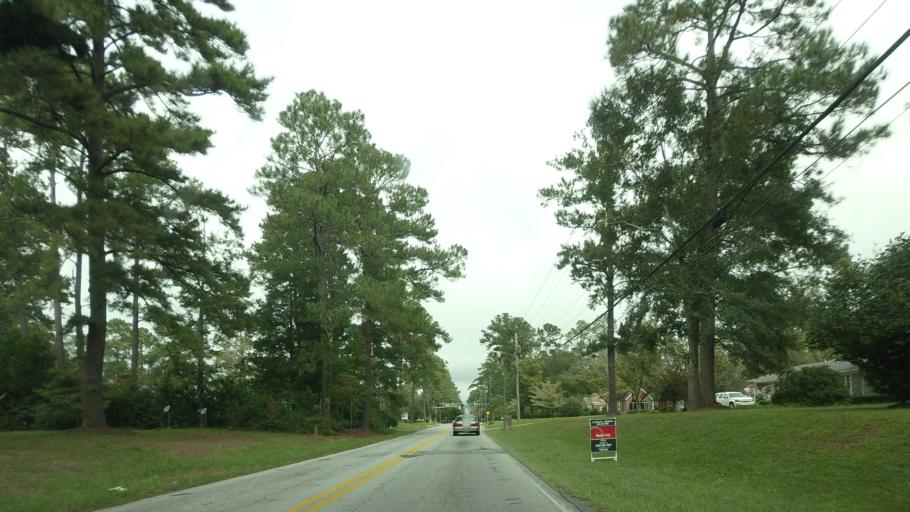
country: US
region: Georgia
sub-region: Lowndes County
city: Remerton
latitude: 30.8581
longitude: -83.2925
